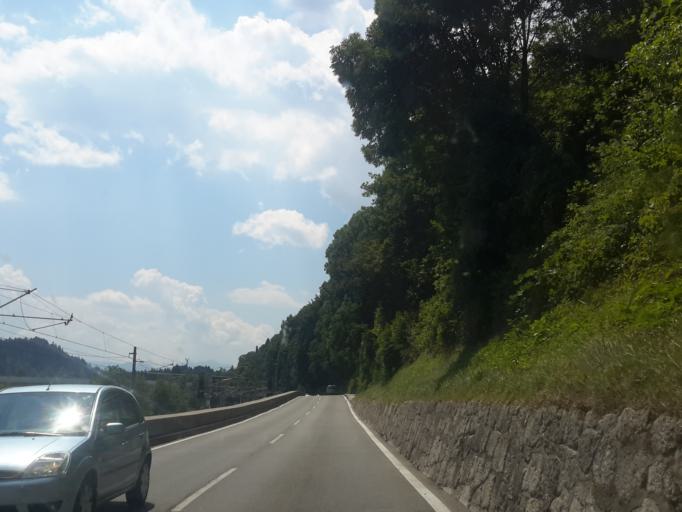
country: AT
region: Tyrol
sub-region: Politischer Bezirk Kufstein
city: Kufstein
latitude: 47.5944
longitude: 12.1683
